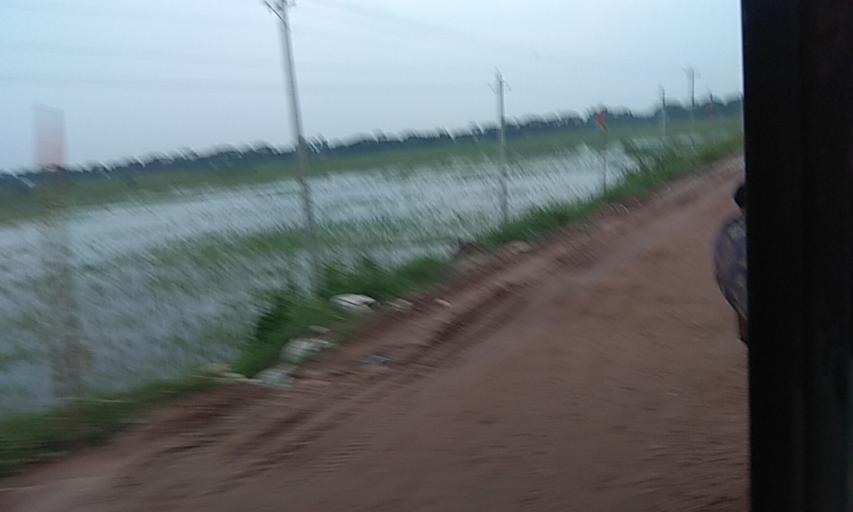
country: BD
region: Dhaka
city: Char Bhadrasan
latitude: 23.3838
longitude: 89.9986
